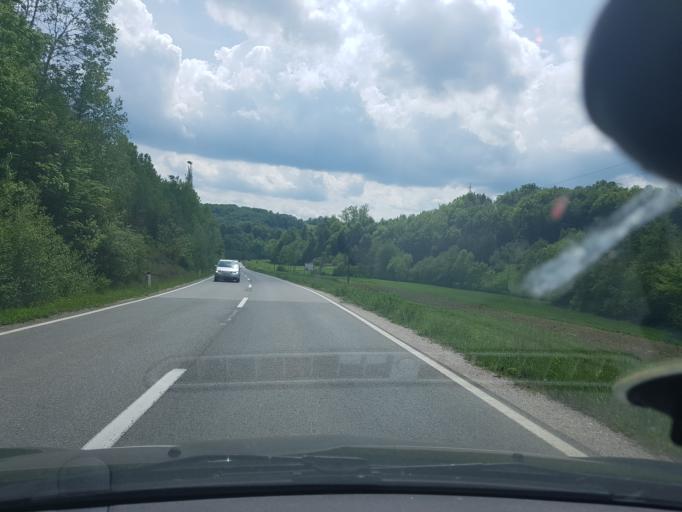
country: SI
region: Rogaska Slatina
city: Rogaska Slatina
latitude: 46.2481
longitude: 15.6044
